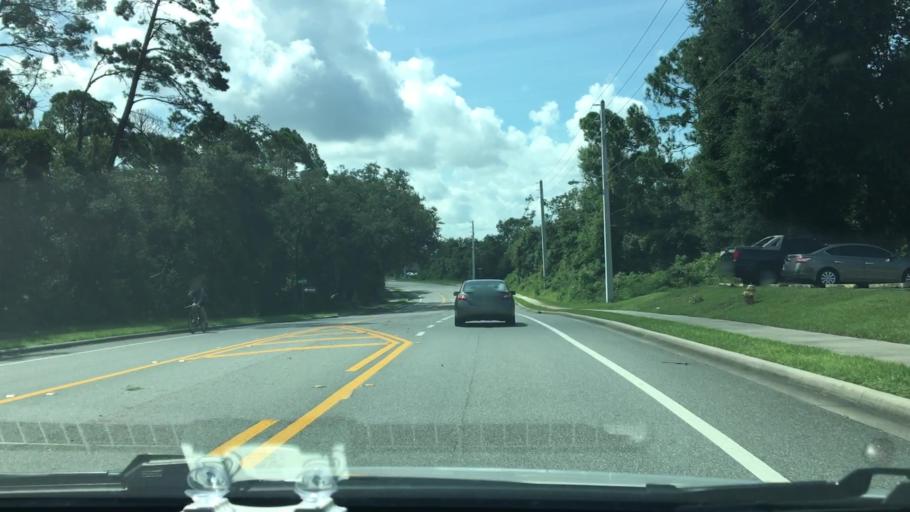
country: US
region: Florida
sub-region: Volusia County
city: Deltona
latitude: 28.8828
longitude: -81.2091
